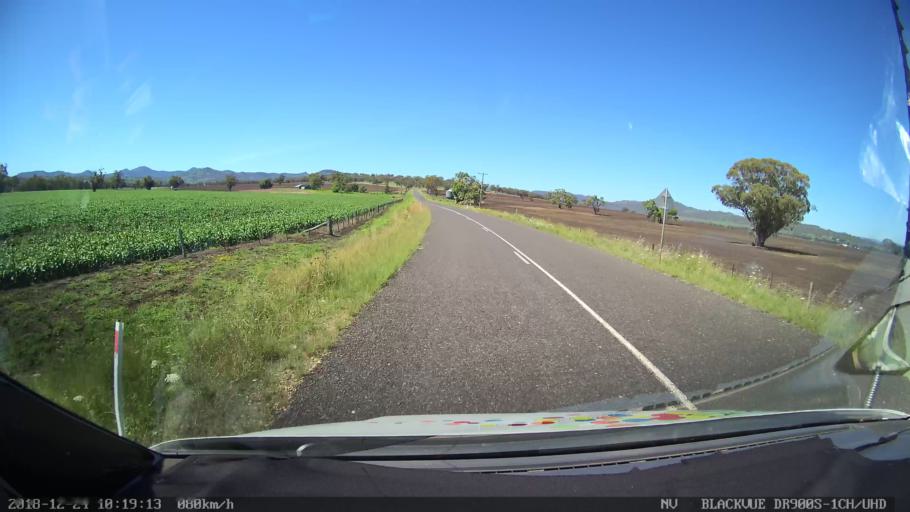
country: AU
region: New South Wales
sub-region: Liverpool Plains
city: Quirindi
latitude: -31.7277
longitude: 150.5659
